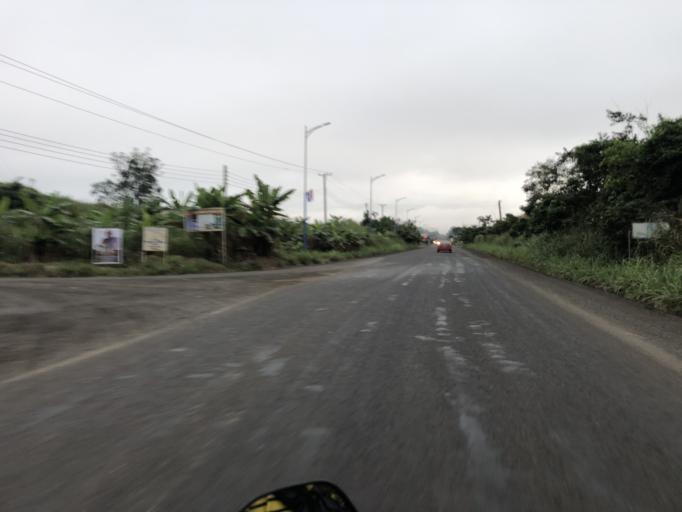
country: GH
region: Eastern
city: Koforidua
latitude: 6.1889
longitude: -0.3554
